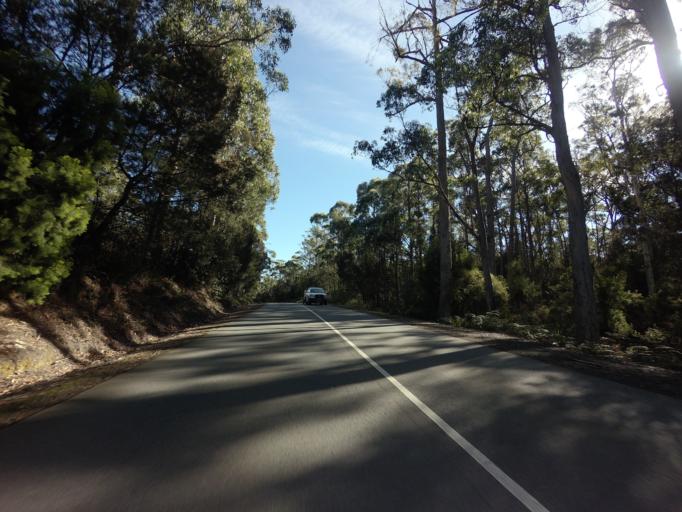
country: AU
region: Tasmania
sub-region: Clarence
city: Sandford
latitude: -43.0581
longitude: 147.8523
